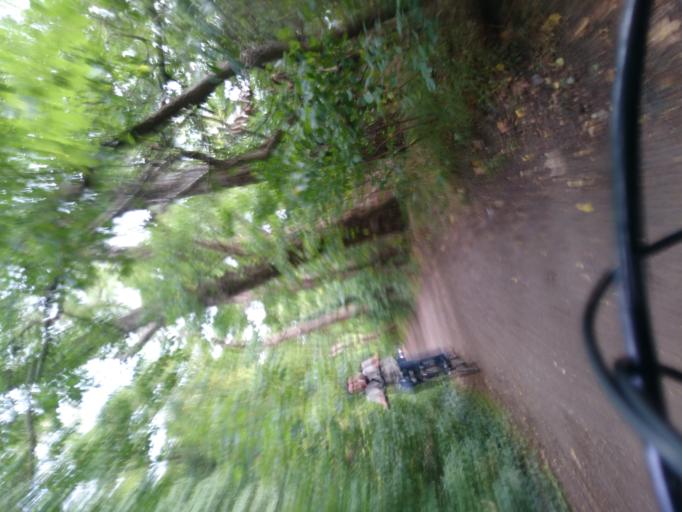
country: DE
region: Mecklenburg-Vorpommern
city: Elmenhorst
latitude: 54.1747
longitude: 12.0273
